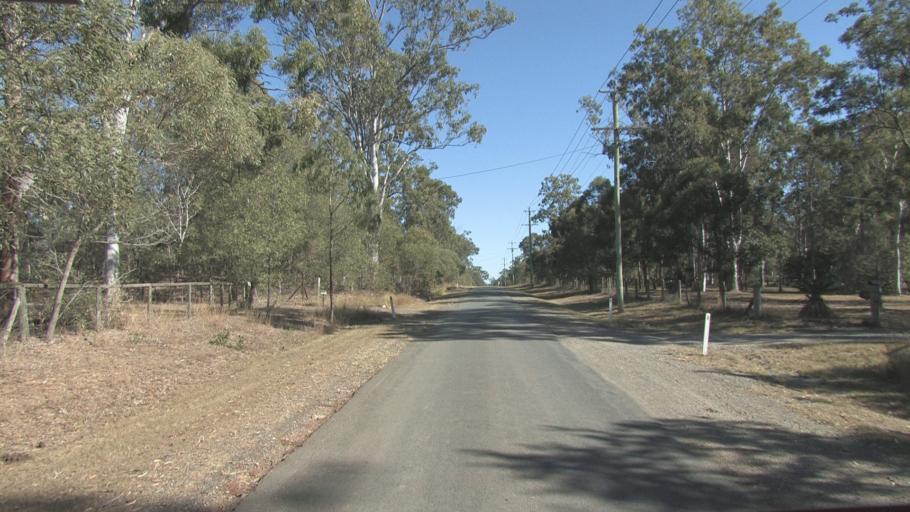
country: AU
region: Queensland
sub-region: Logan
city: North Maclean
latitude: -27.7997
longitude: 153.0537
